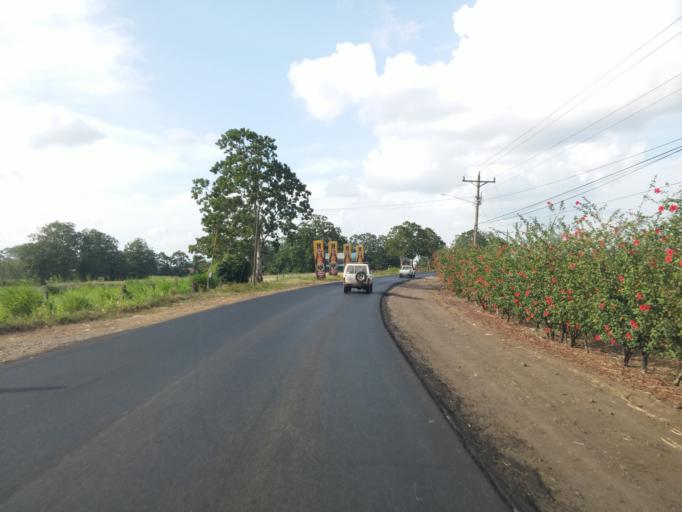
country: CR
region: Alajuela
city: Quesada
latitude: 10.4365
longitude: -84.4676
